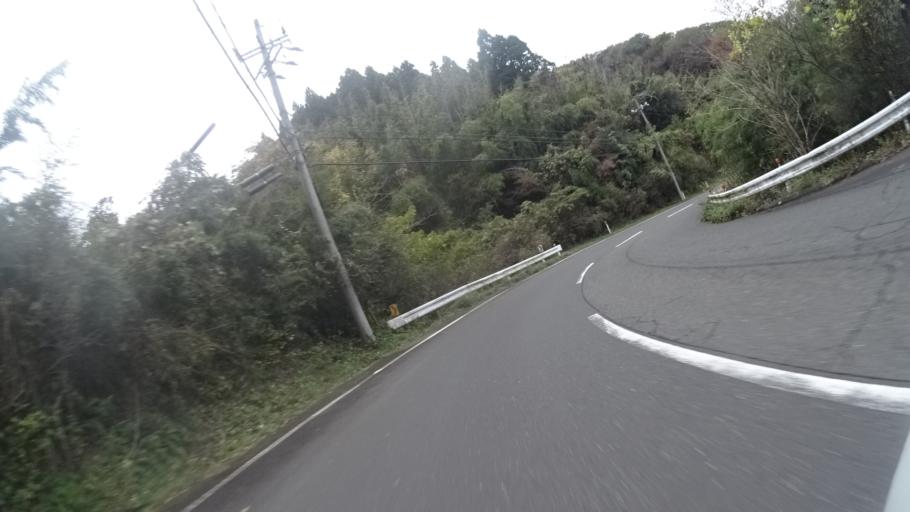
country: JP
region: Kyoto
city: Maizuru
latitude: 35.5536
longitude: 135.4546
